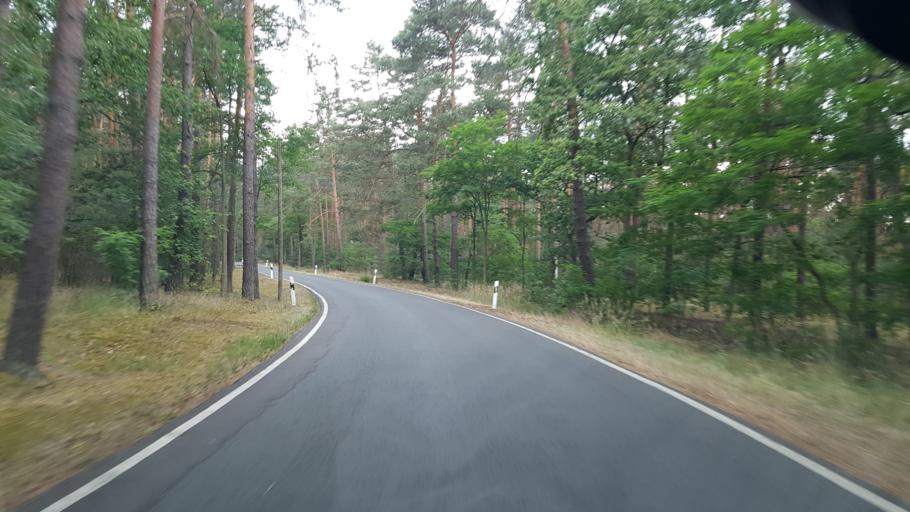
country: DE
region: Brandenburg
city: Kasel-Golzig
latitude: 51.9744
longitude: 13.6883
